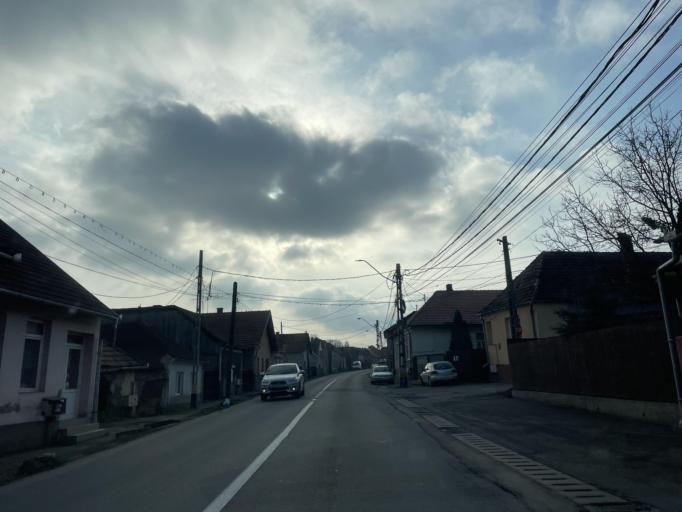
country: RO
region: Mures
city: Reghin-Sat
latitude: 46.7885
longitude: 24.7110
